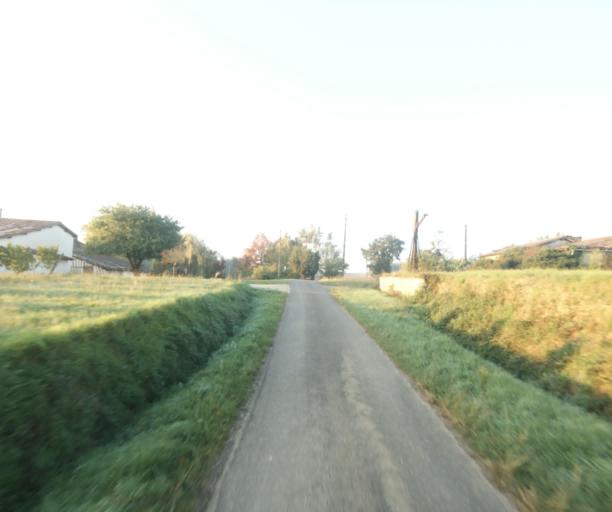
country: FR
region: Midi-Pyrenees
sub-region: Departement du Gers
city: Eauze
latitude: 43.7891
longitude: 0.1788
